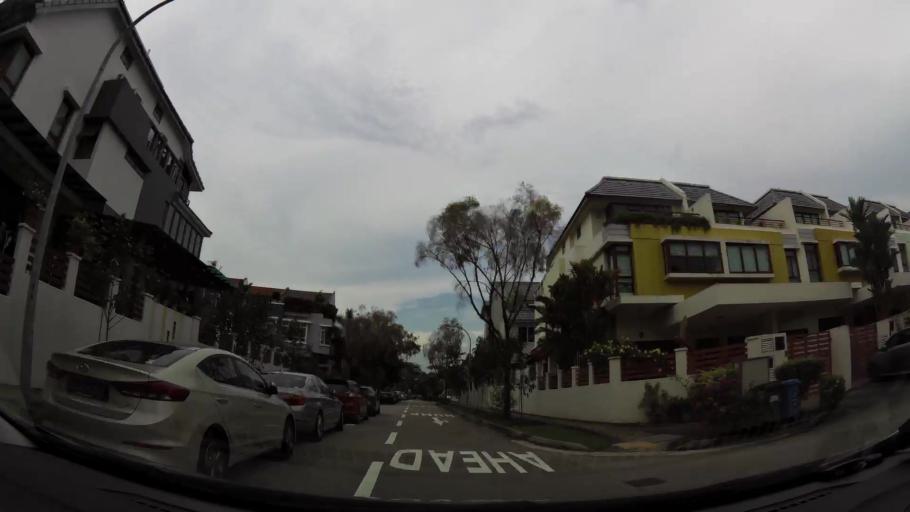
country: SG
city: Singapore
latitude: 1.3609
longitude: 103.8663
